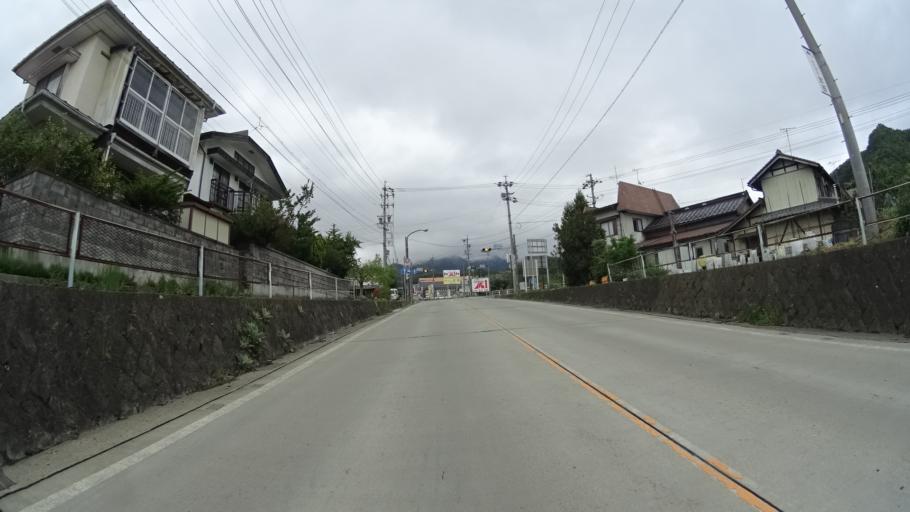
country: JP
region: Nagano
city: Nakano
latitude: 36.7583
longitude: 138.3872
